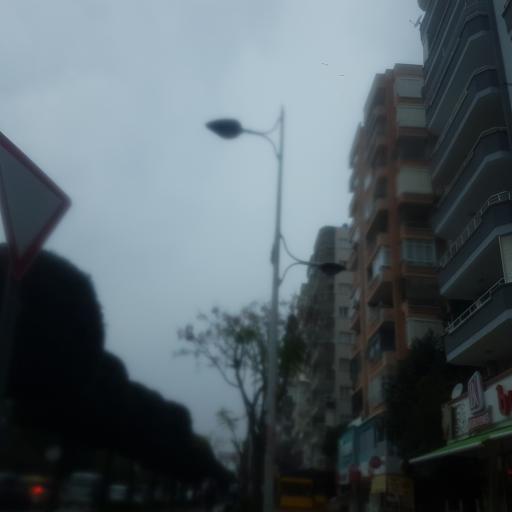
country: TR
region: Adana
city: Adana
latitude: 37.0487
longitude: 35.2850
